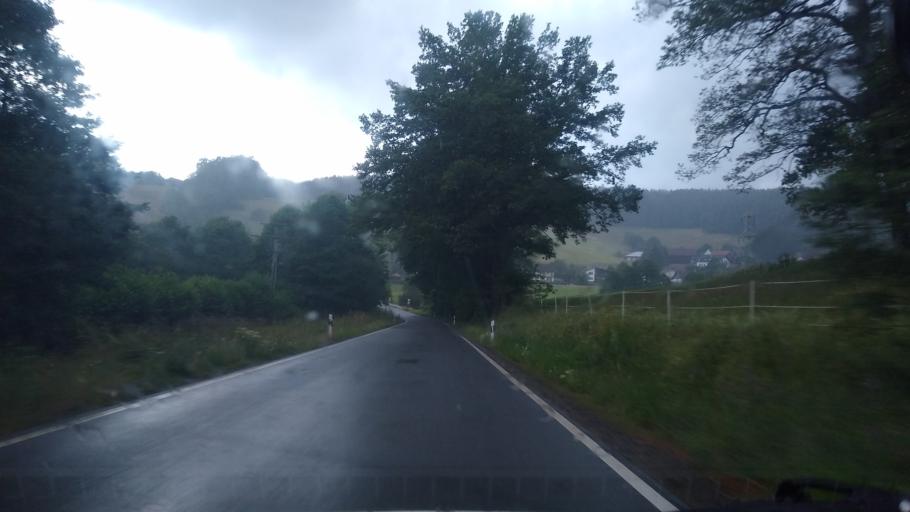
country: DE
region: Hesse
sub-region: Regierungsbezirk Darmstadt
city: Erbach
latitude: 49.6508
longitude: 8.9346
